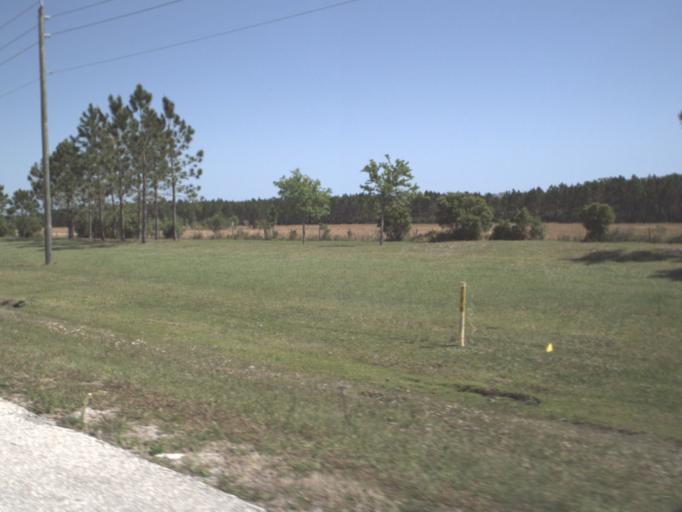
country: US
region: Florida
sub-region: Flagler County
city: Palm Coast
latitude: 29.5933
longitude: -81.2813
